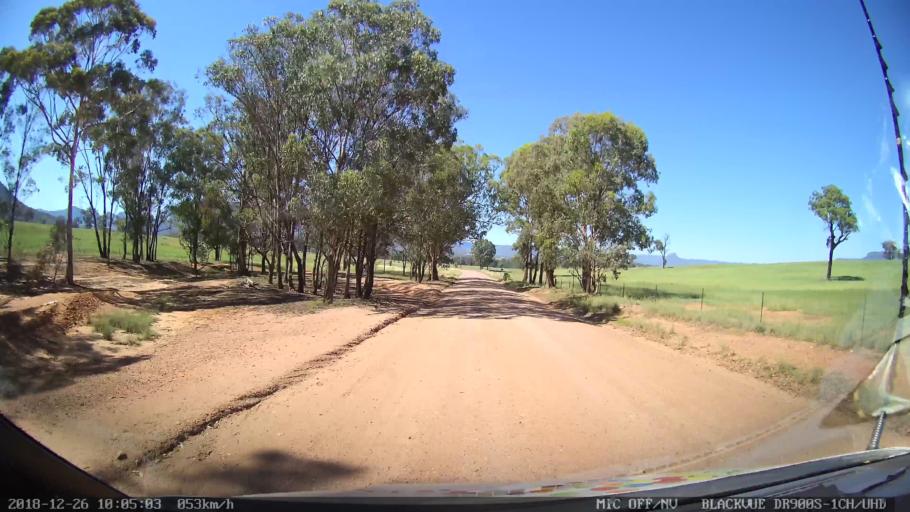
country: AU
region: New South Wales
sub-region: Mid-Western Regional
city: Kandos
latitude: -33.0753
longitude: 150.2123
